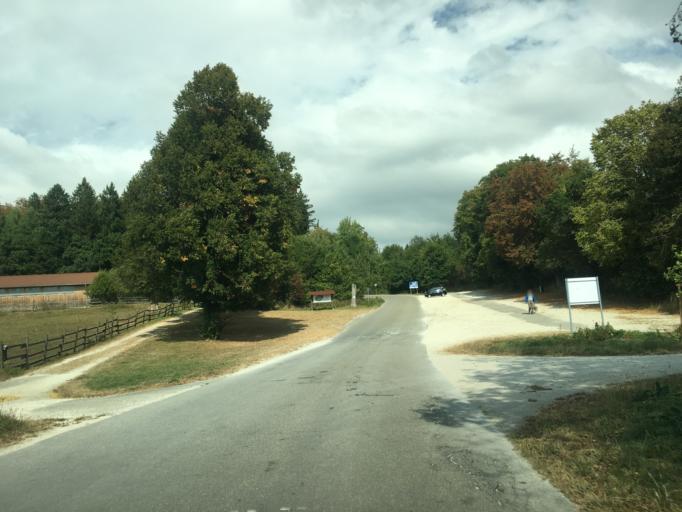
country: DE
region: Baden-Wuerttemberg
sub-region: Tuebingen Region
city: Trochtelfingen
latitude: 48.3676
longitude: 9.2205
